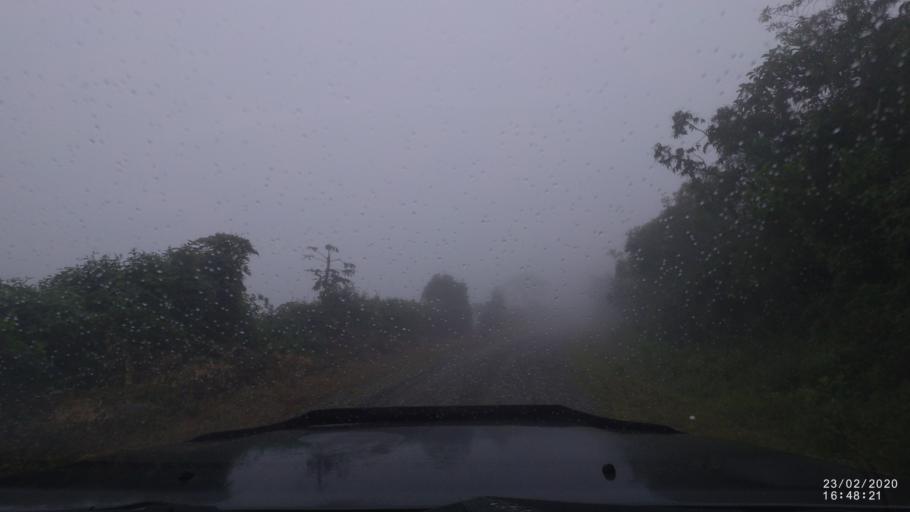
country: BO
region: Cochabamba
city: Colomi
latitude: -17.0927
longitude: -65.9911
